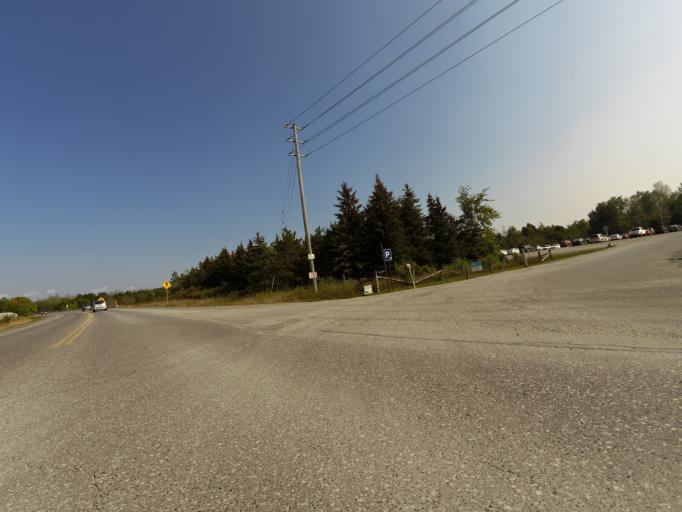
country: CA
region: Ontario
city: Bells Corners
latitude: 45.3234
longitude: -75.8049
